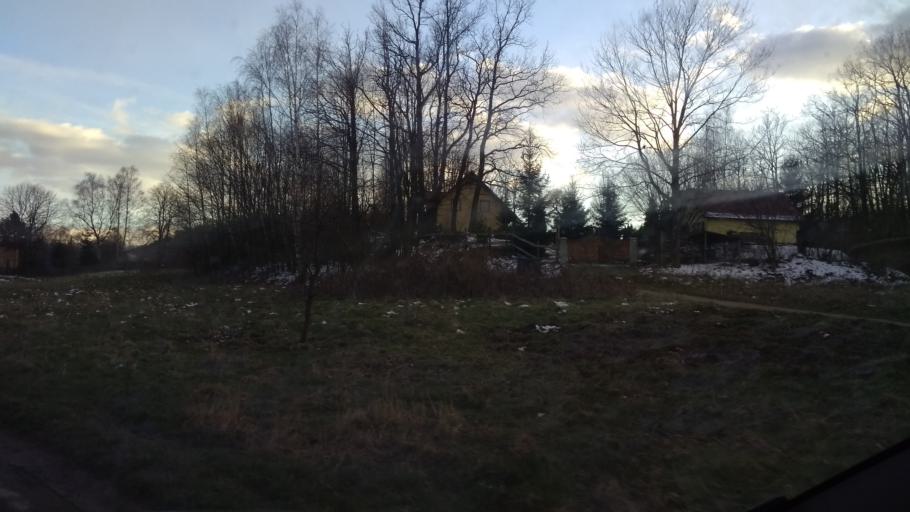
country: PL
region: Lower Silesian Voivodeship
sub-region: Powiat jeleniogorski
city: Sosnowka
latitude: 50.8444
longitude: 15.7381
